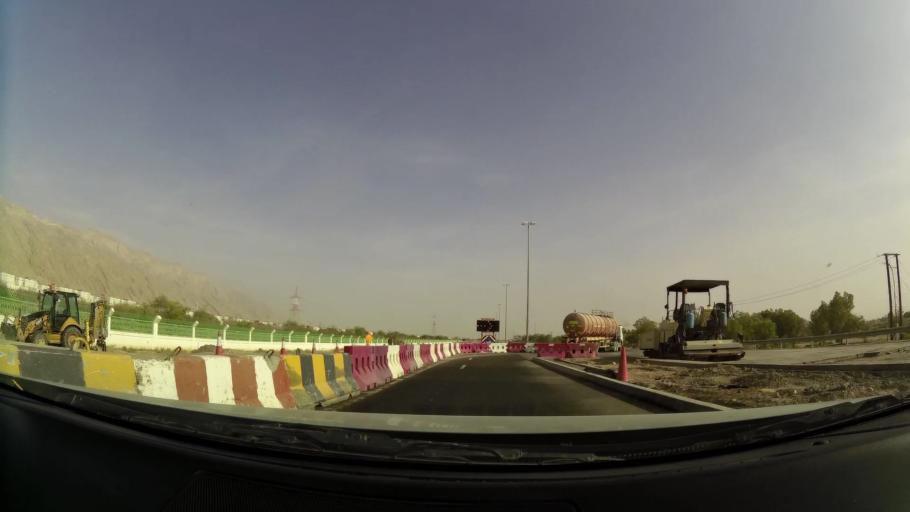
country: AE
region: Abu Dhabi
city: Al Ain
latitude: 24.0764
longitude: 55.7274
